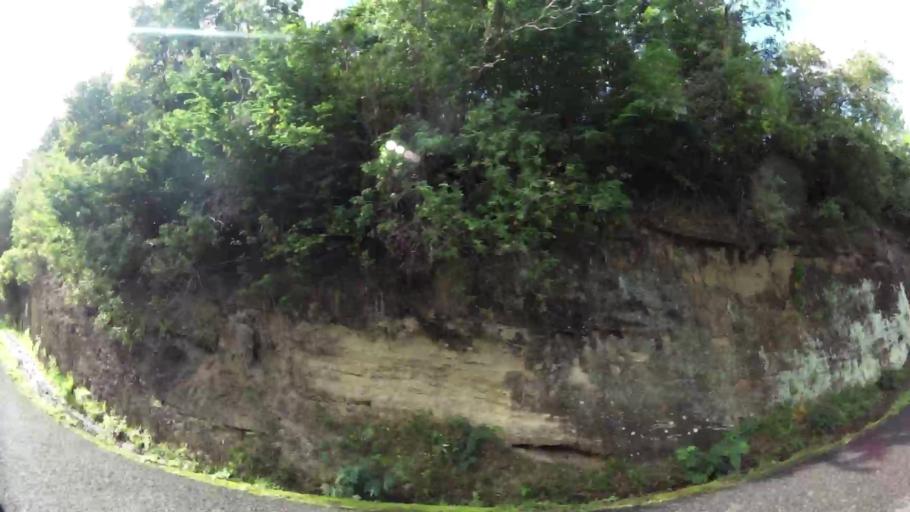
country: LC
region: Anse-la-Raye
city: Canaries
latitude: 13.8978
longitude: -61.0625
